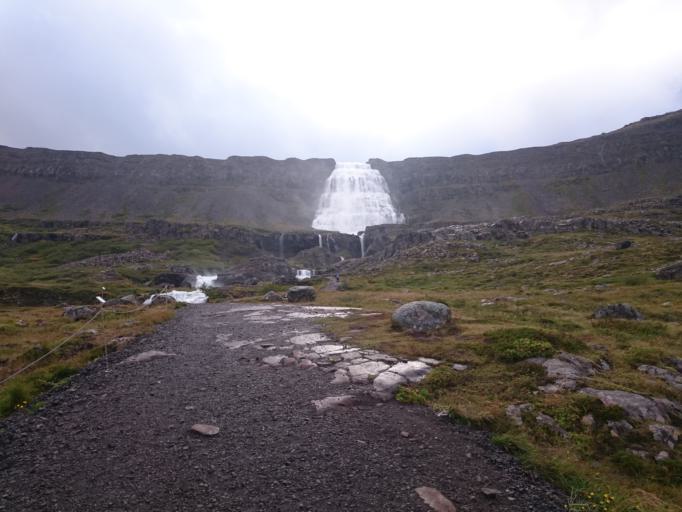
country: IS
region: Westfjords
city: Isafjoerdur
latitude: 65.7359
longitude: -23.2075
